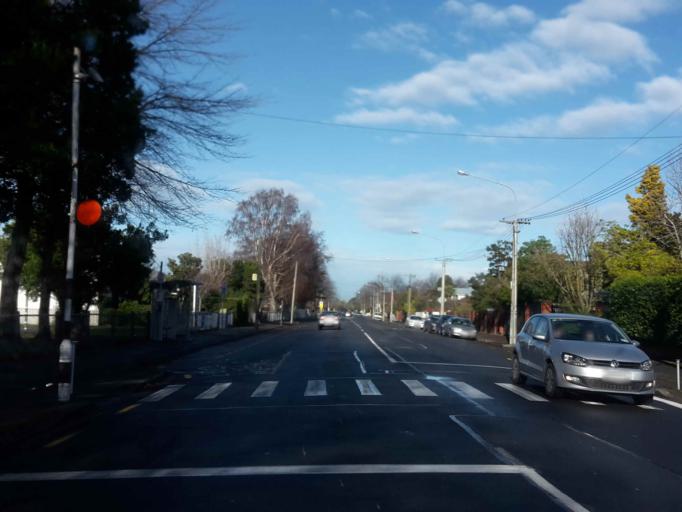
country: NZ
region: Canterbury
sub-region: Christchurch City
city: Christchurch
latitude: -43.5157
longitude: 172.5909
